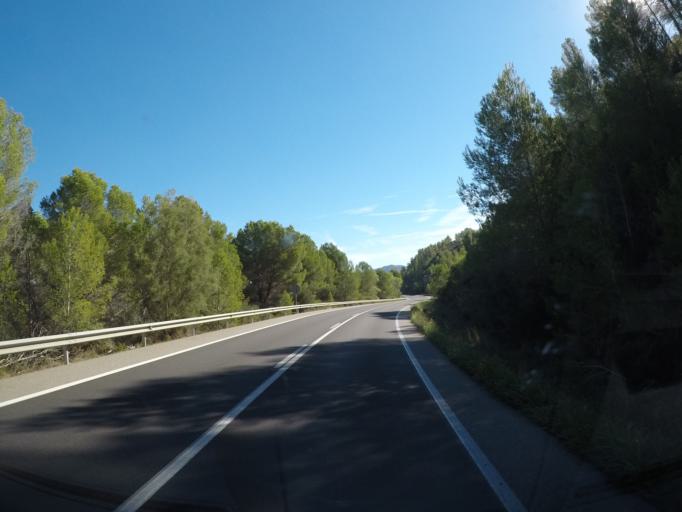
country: ES
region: Catalonia
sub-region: Provincia de Tarragona
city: Miravet
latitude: 41.0319
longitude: 0.6109
